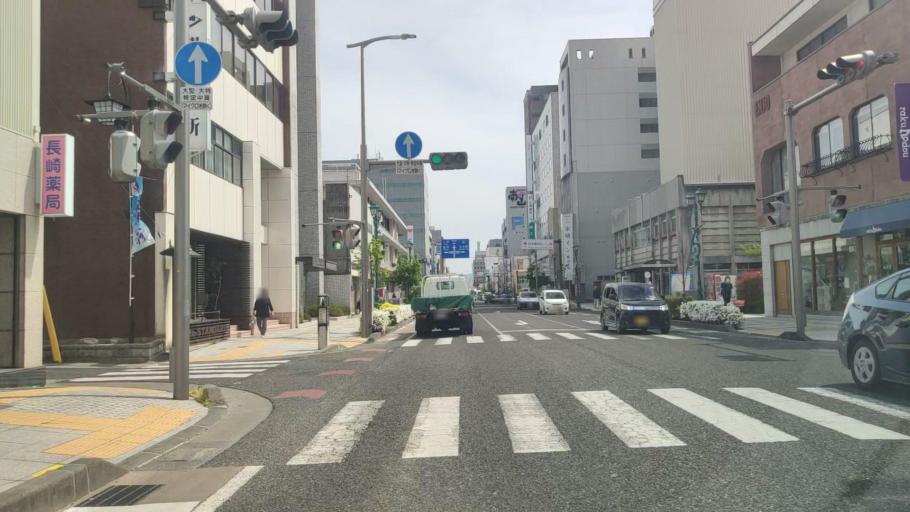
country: JP
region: Nagano
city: Matsumoto
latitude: 36.2325
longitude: 137.9694
